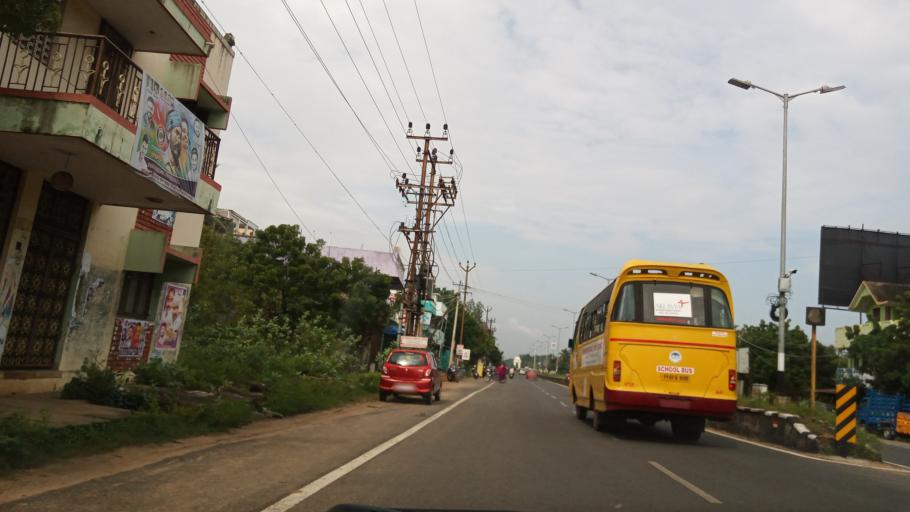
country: IN
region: Tamil Nadu
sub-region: Villupuram
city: Auroville
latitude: 12.0357
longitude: 79.8660
